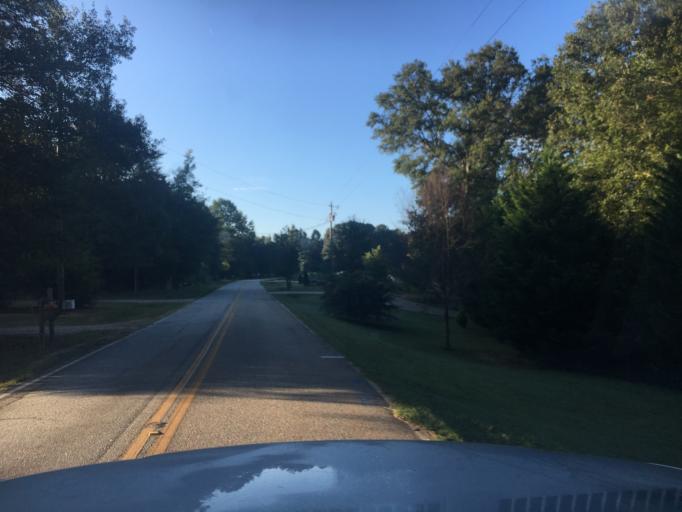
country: US
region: South Carolina
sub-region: Spartanburg County
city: Woodruff
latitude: 34.7617
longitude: -81.9617
